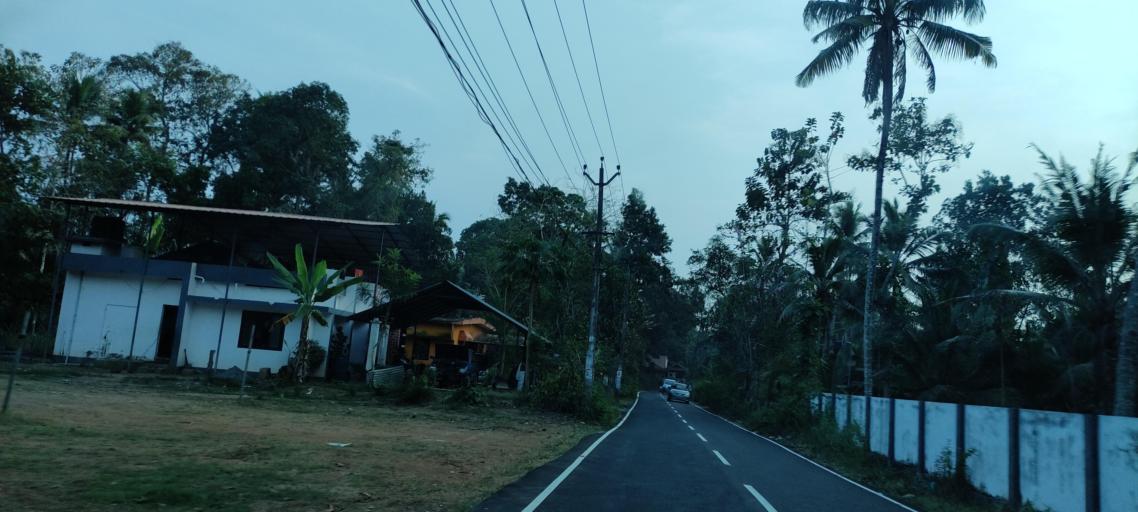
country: IN
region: Kerala
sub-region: Alappuzha
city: Mavelikara
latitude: 9.2742
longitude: 76.5518
